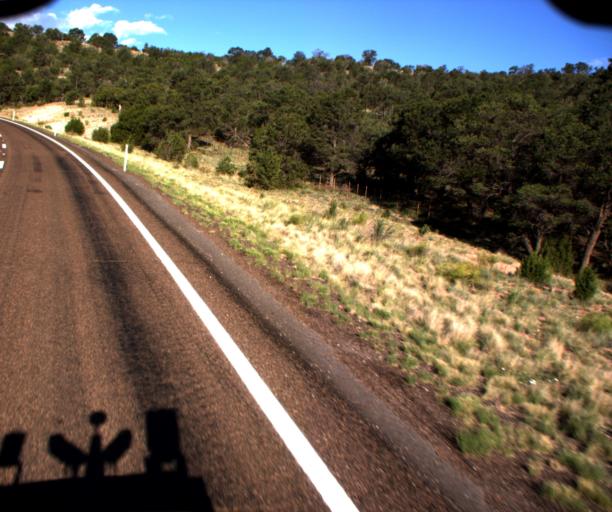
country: US
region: Arizona
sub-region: Apache County
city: Eagar
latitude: 34.0999
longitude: -109.2178
